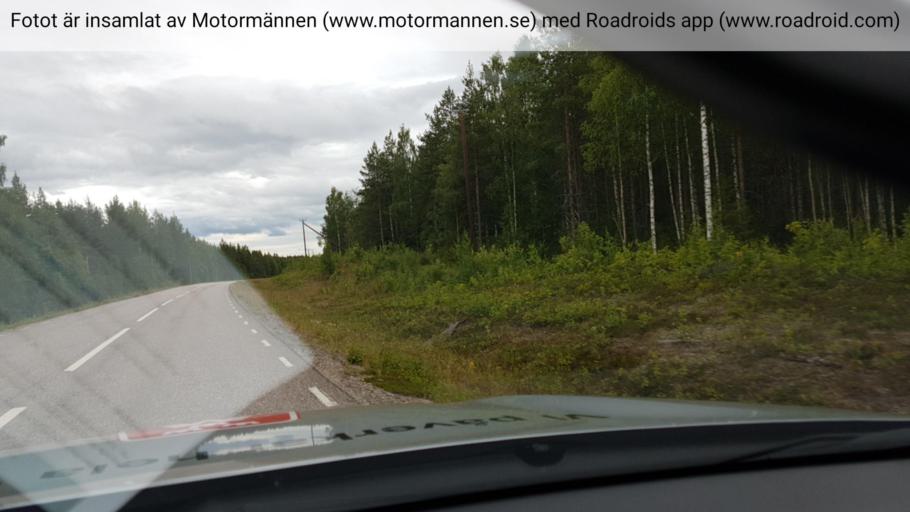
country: SE
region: Norrbotten
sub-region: Overkalix Kommun
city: OEverkalix
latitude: 66.7604
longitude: 22.9058
